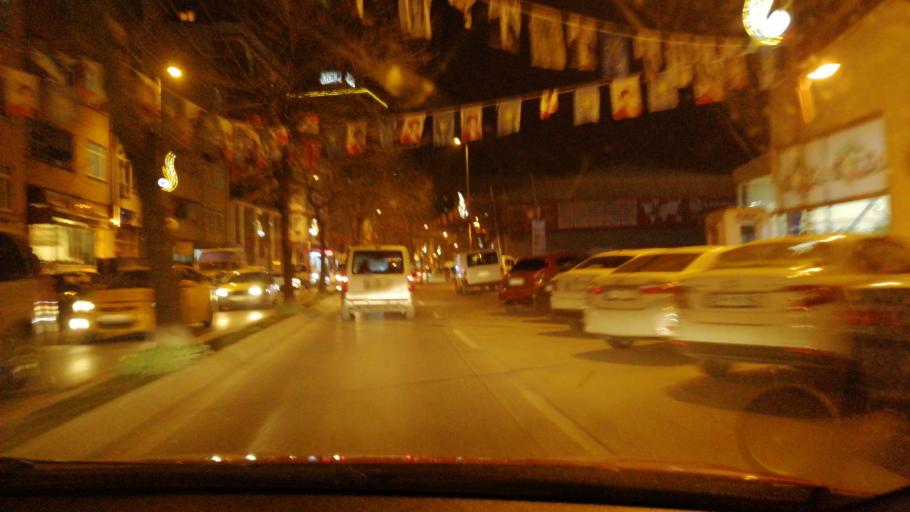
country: TR
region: Istanbul
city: Sisli
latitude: 41.0826
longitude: 28.9737
